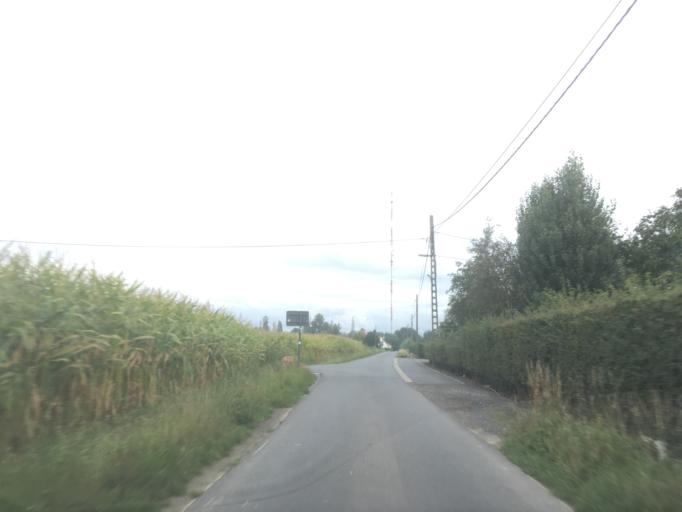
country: BE
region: Flanders
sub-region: Provincie West-Vlaanderen
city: Pittem
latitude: 51.0144
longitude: 3.2257
